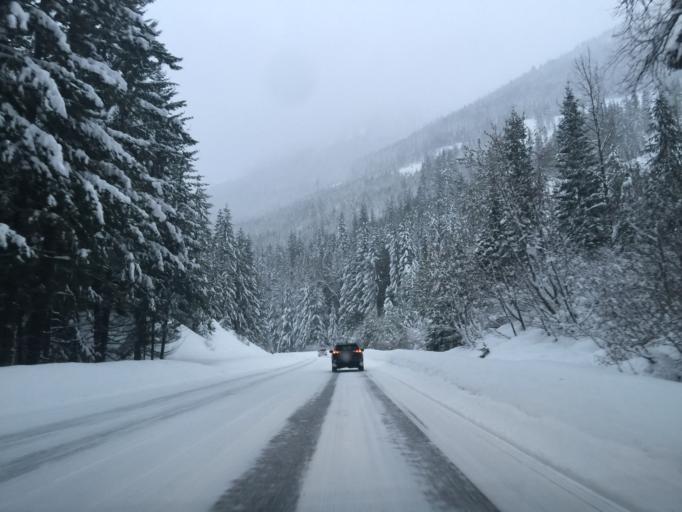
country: US
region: Washington
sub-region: Chelan County
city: Leavenworth
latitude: 47.7674
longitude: -120.9917
